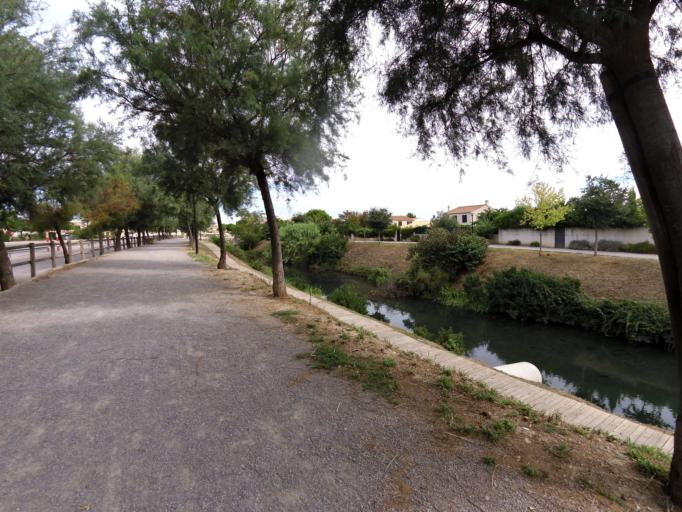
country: FR
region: Languedoc-Roussillon
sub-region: Departement de l'Herault
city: Lunel
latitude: 43.6667
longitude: 4.1278
